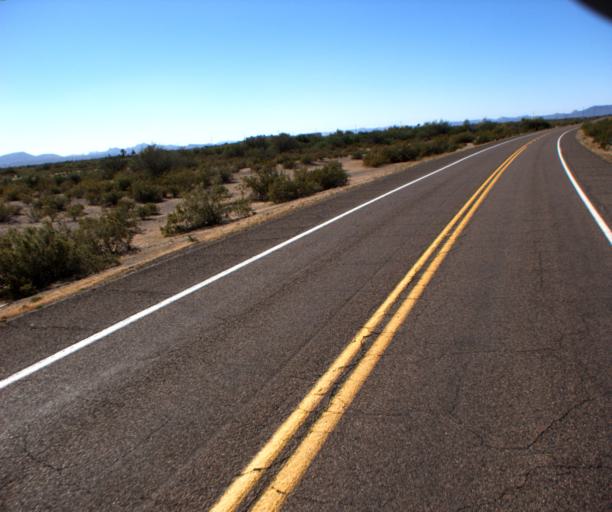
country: US
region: Arizona
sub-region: Maricopa County
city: Gila Bend
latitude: 32.9364
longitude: -112.7335
